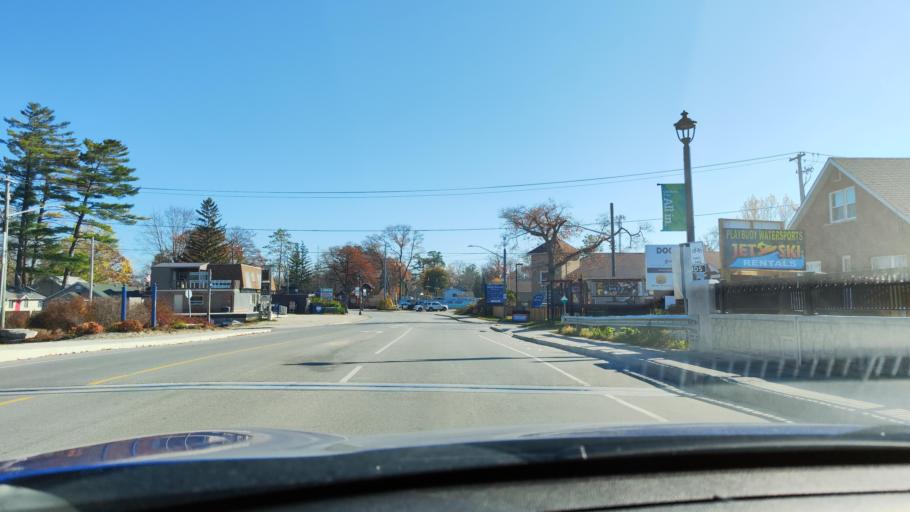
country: CA
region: Ontario
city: Wasaga Beach
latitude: 44.5231
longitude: -80.0168
